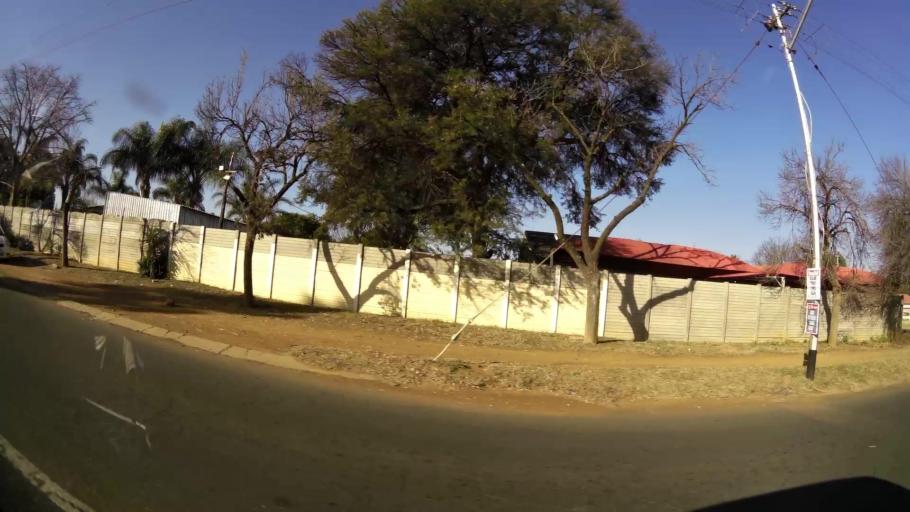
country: ZA
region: Gauteng
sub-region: City of Tshwane Metropolitan Municipality
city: Pretoria
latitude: -25.7111
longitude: 28.2426
